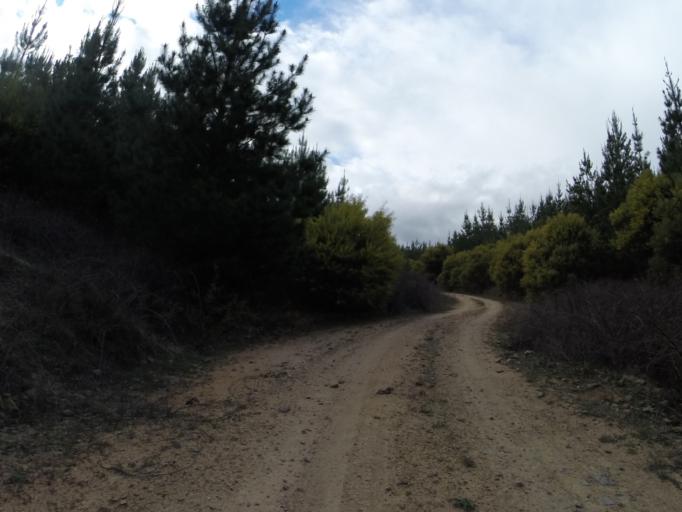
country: AU
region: Australian Capital Territory
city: Macquarie
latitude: -35.3488
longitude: 148.9497
